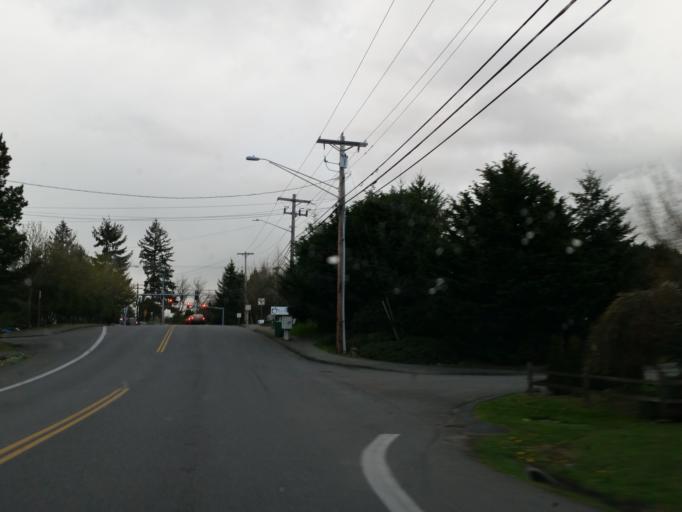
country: US
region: Washington
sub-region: Snohomish County
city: Alderwood Manor
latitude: 47.8123
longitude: -122.2793
